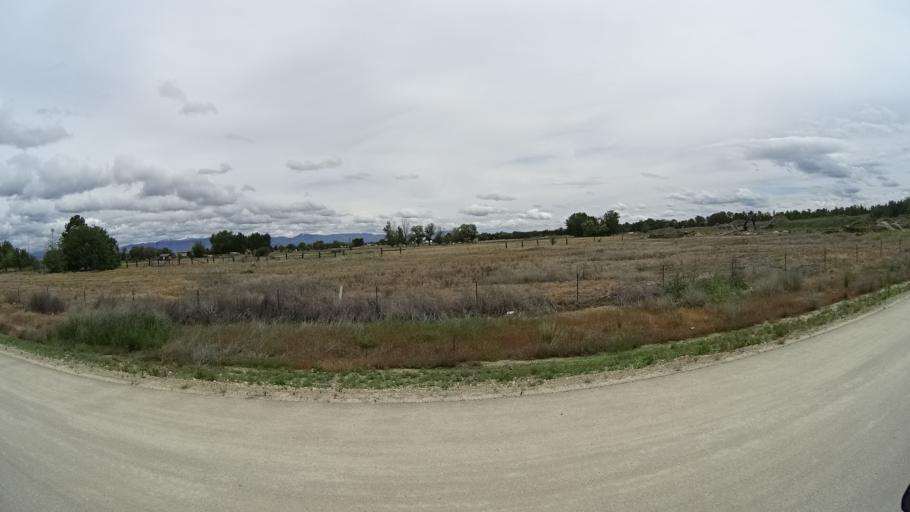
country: US
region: Idaho
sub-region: Ada County
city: Star
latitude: 43.6888
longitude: -116.4599
